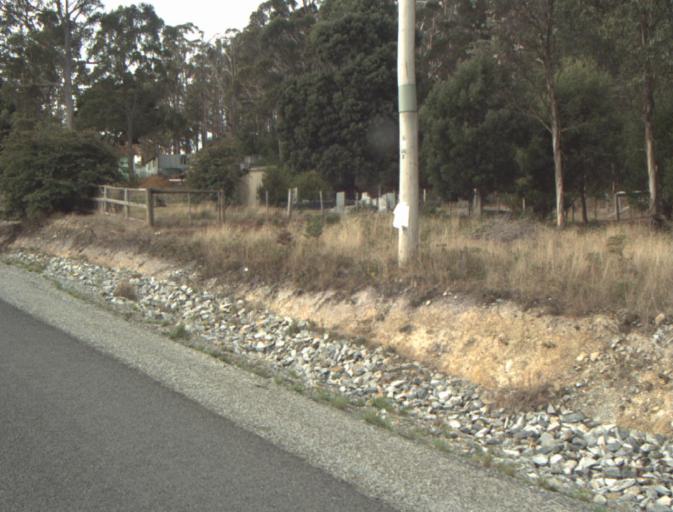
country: AU
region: Tasmania
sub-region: Launceston
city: Mayfield
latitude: -41.1943
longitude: 147.1817
